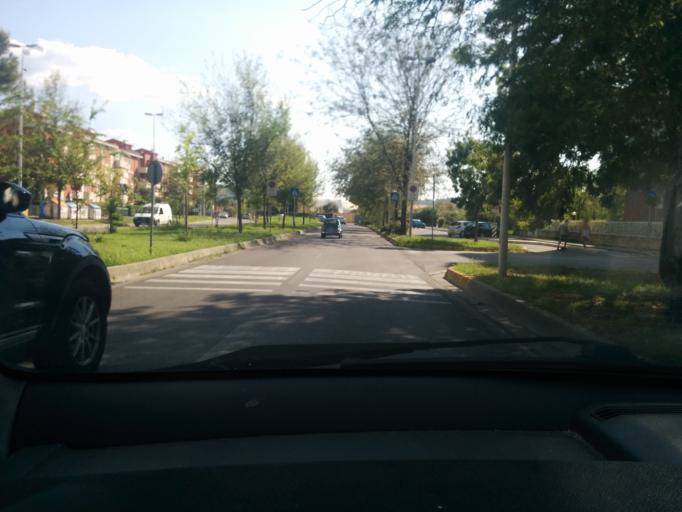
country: IT
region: Tuscany
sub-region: Province of Florence
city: Fiesole
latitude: 43.7742
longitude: 11.3001
